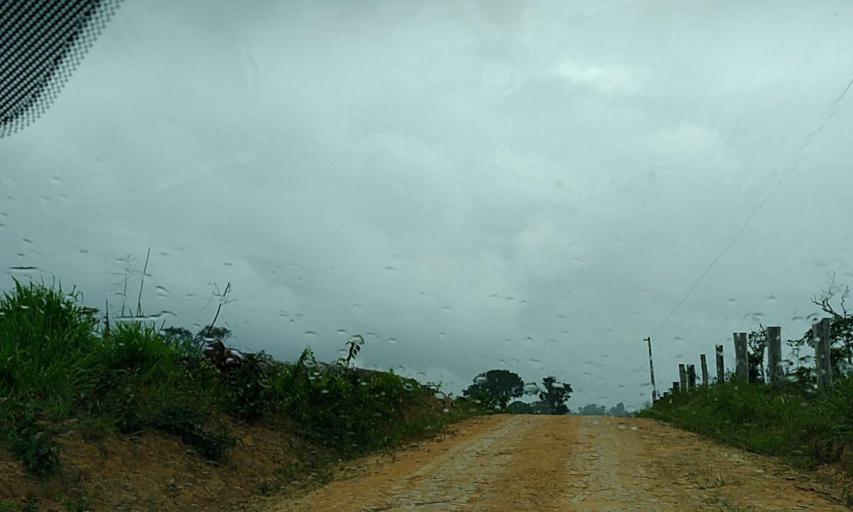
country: BR
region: Para
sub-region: Altamira
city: Altamira
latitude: -2.9495
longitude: -52.9009
